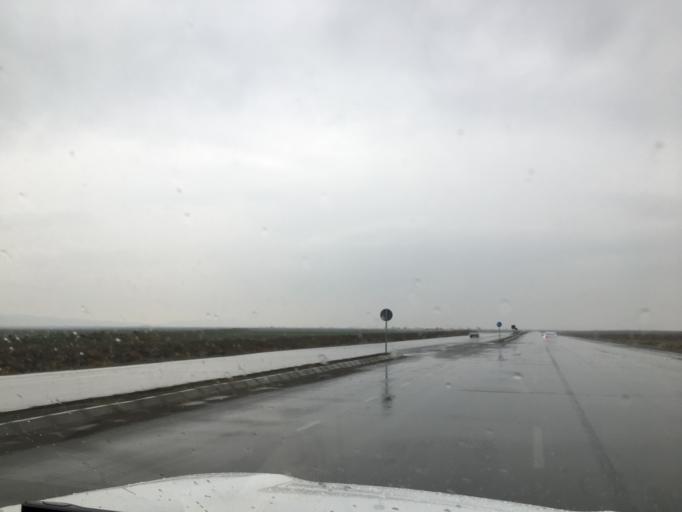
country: TM
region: Ahal
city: Annau
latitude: 37.8053
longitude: 58.7918
